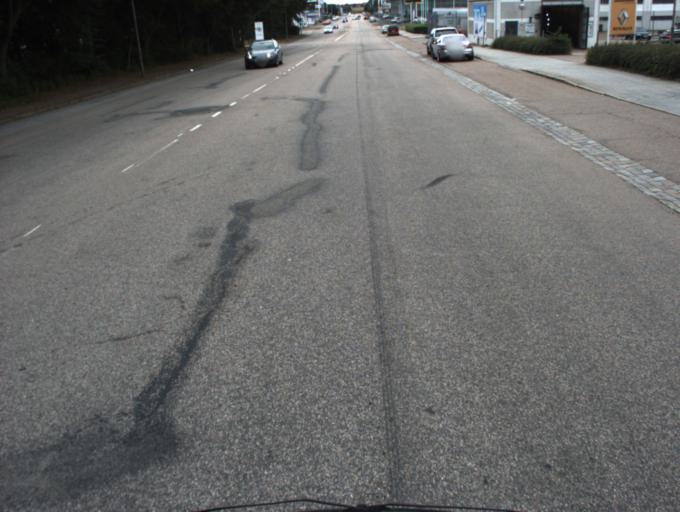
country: SE
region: Skane
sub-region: Helsingborg
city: Helsingborg
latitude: 56.0698
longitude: 12.7185
